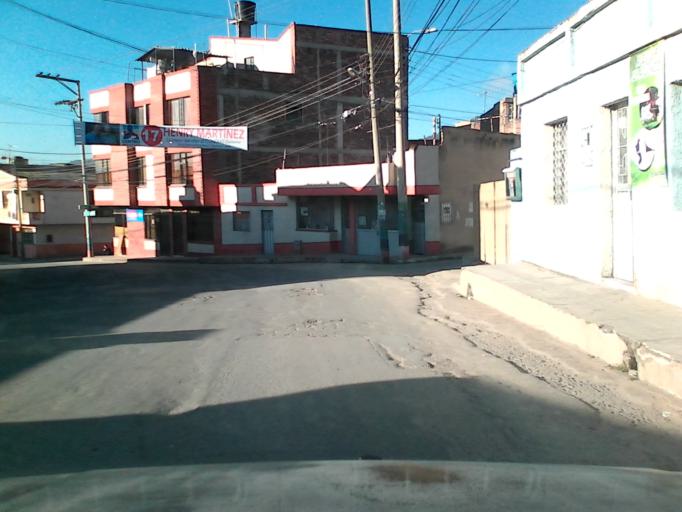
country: CO
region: Boyaca
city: Duitama
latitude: 5.8365
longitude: -73.0370
